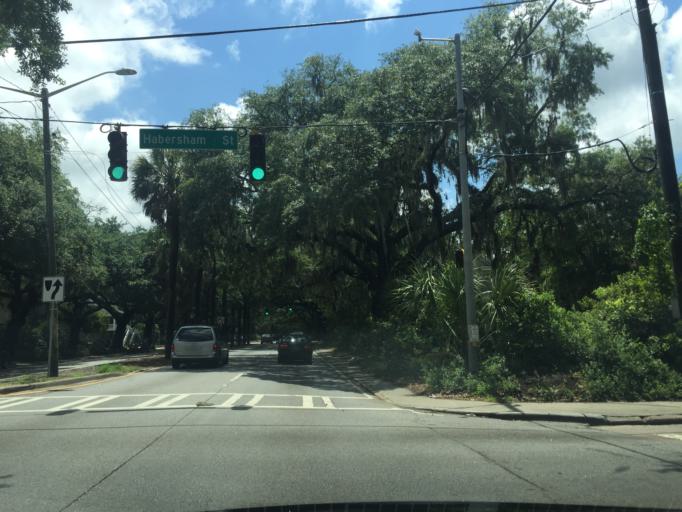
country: US
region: Georgia
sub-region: Chatham County
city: Savannah
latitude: 32.0514
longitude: -81.0976
